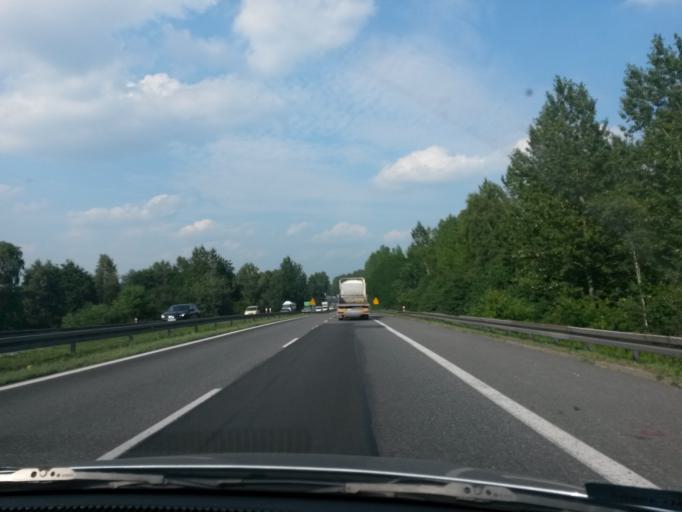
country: PL
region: Silesian Voivodeship
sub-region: Myslowice
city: Myslowice
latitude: 50.2477
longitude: 19.1772
